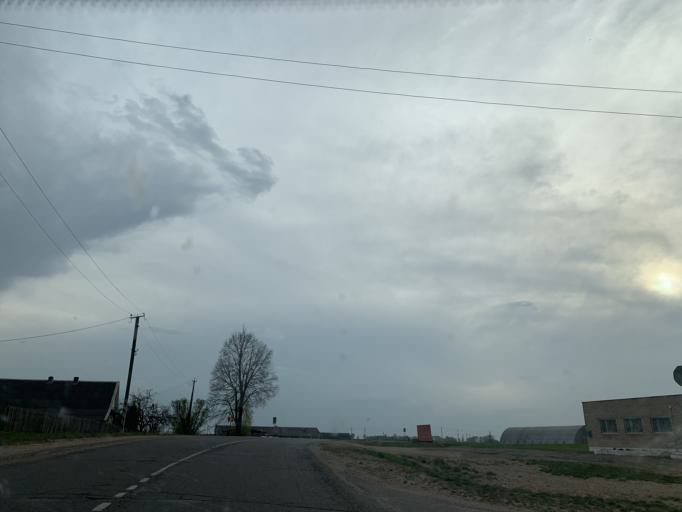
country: BY
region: Minsk
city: Kapyl'
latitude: 53.2942
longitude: 27.0338
